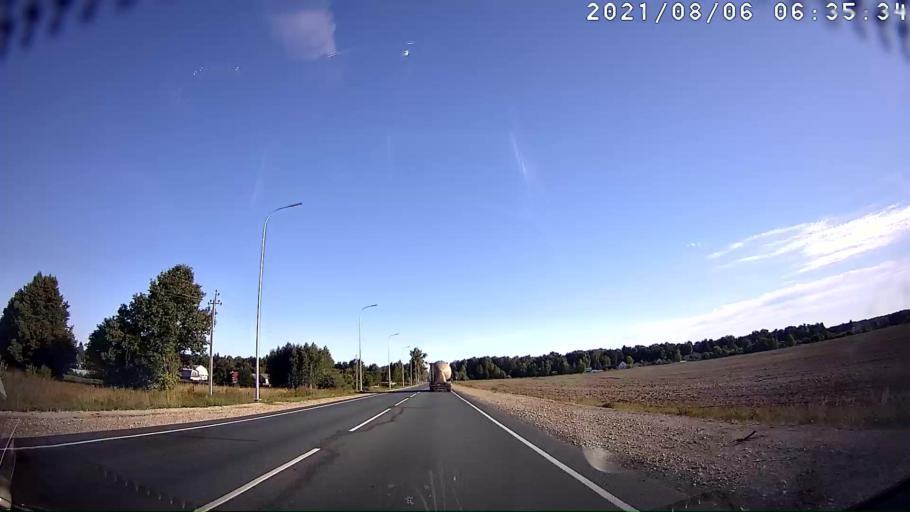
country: RU
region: Mariy-El
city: Suslonger
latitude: 56.2203
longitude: 48.2358
